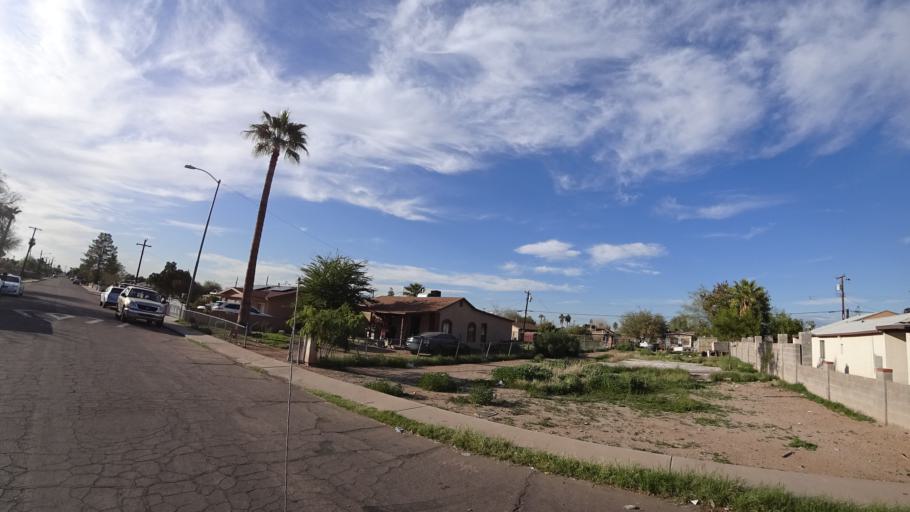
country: US
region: Arizona
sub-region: Maricopa County
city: Phoenix
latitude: 33.4548
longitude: -112.1208
